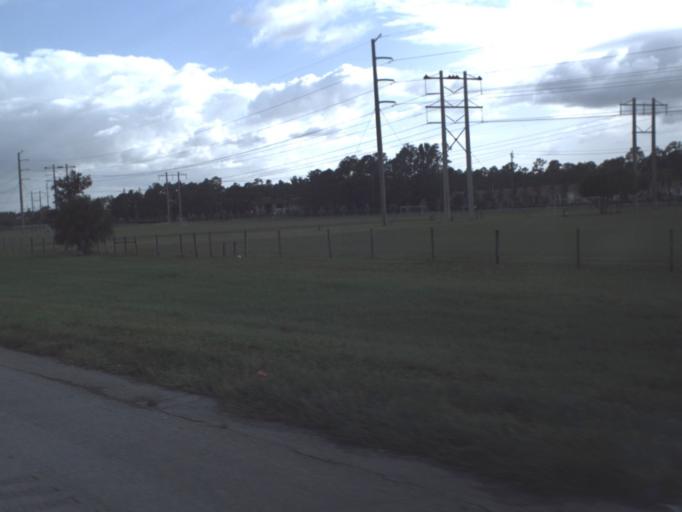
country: US
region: Florida
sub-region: Lee County
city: Bonita Springs
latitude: 26.3511
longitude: -81.7548
